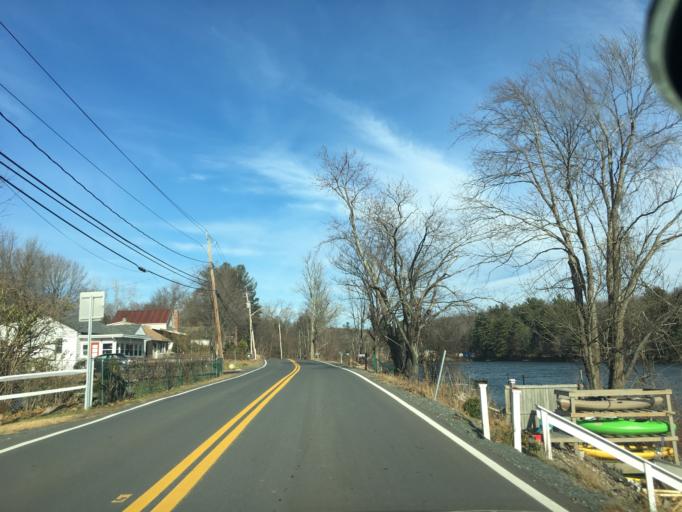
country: US
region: New York
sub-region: Rensselaer County
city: Averill Park
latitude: 42.6178
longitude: -73.5679
